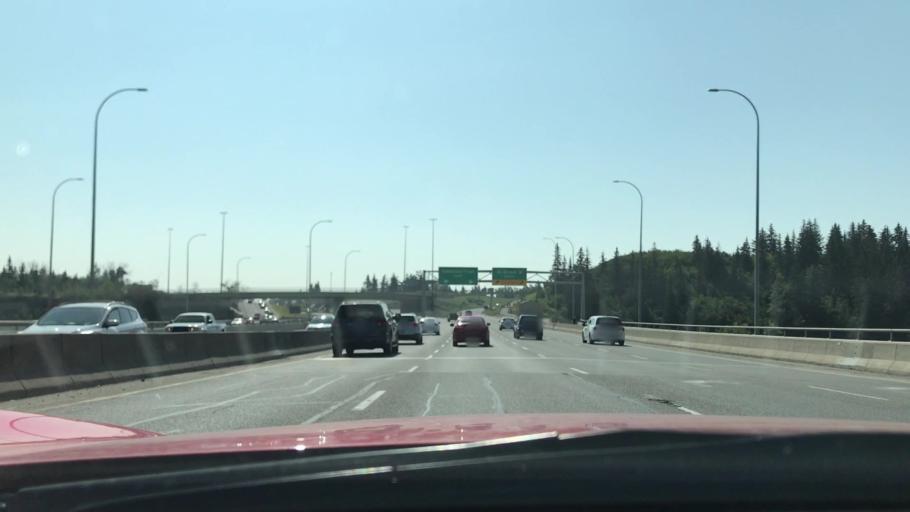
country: CA
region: Alberta
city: Calgary
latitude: 50.9958
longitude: -114.1007
